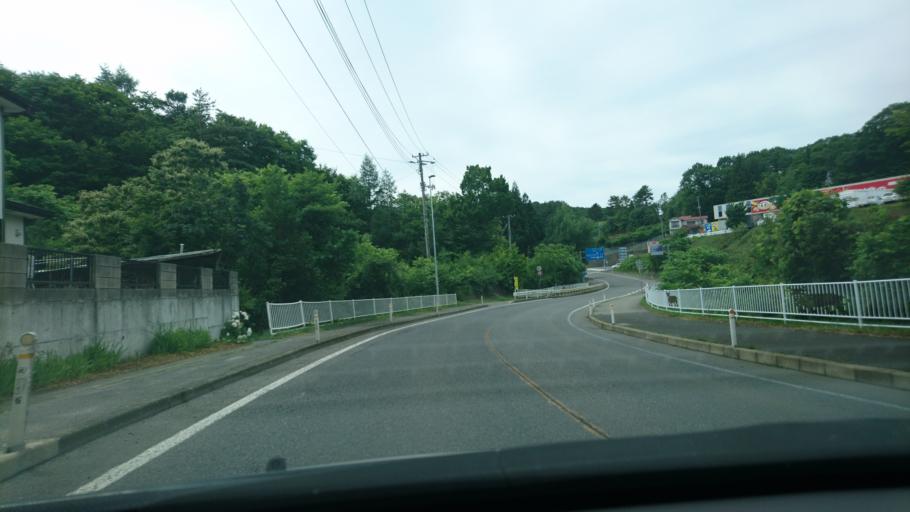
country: JP
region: Iwate
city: Miyako
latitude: 39.9297
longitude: 141.8946
